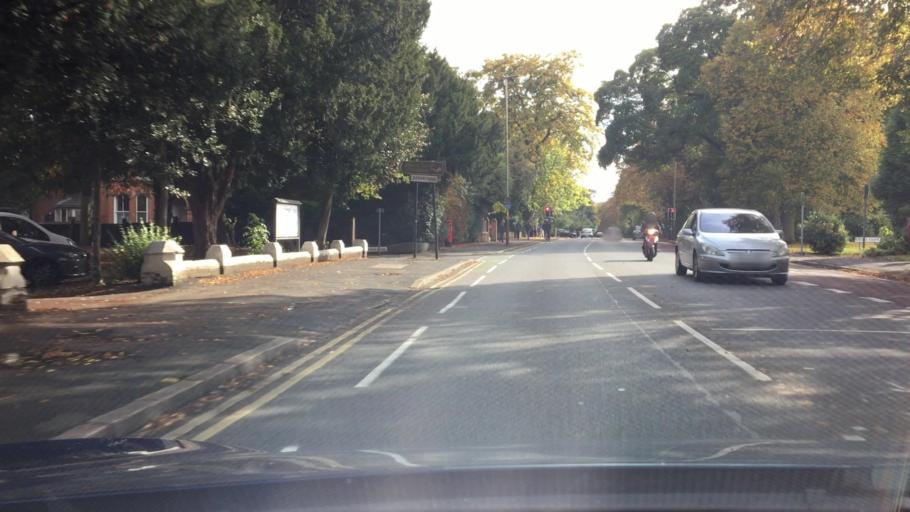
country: GB
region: England
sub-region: City of Leicester
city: Leicester
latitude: 52.6221
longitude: -1.1130
